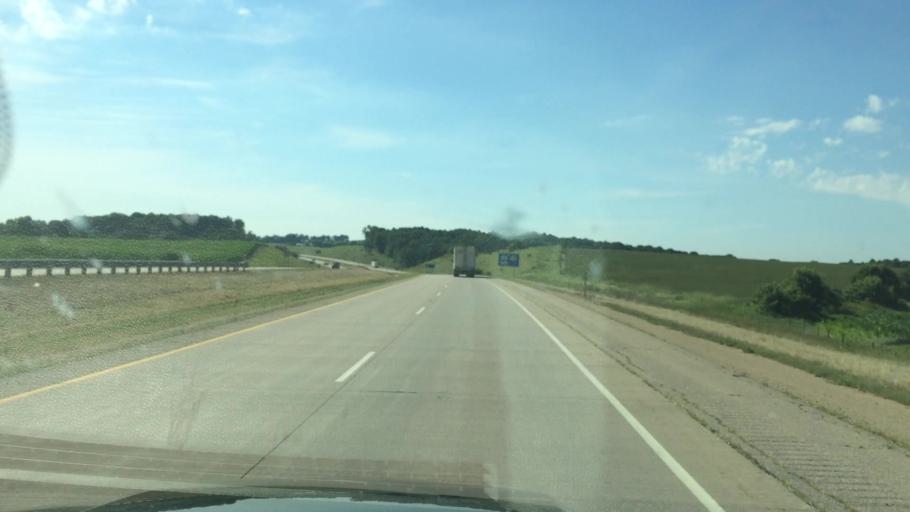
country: US
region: Wisconsin
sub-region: Shawano County
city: Bonduel
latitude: 44.7345
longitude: -88.4617
